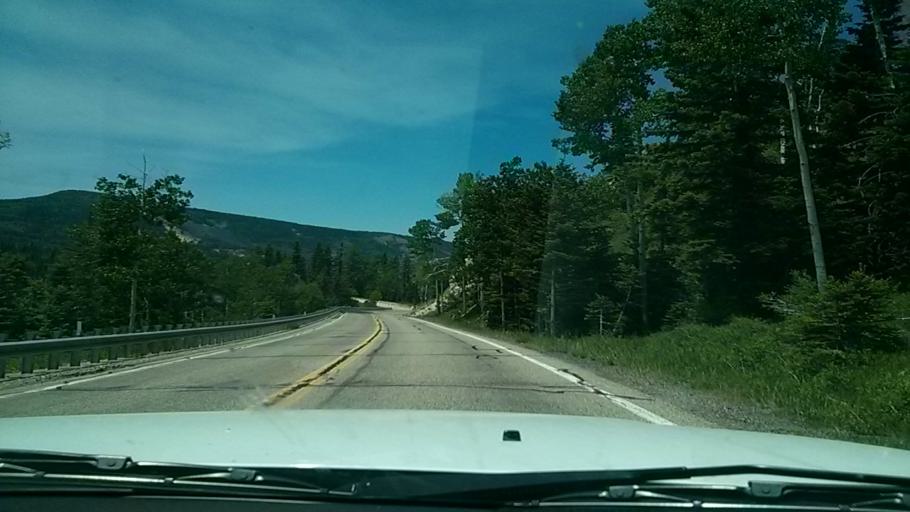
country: US
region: Utah
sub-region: Iron County
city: Cedar City
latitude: 37.5937
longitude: -112.8878
